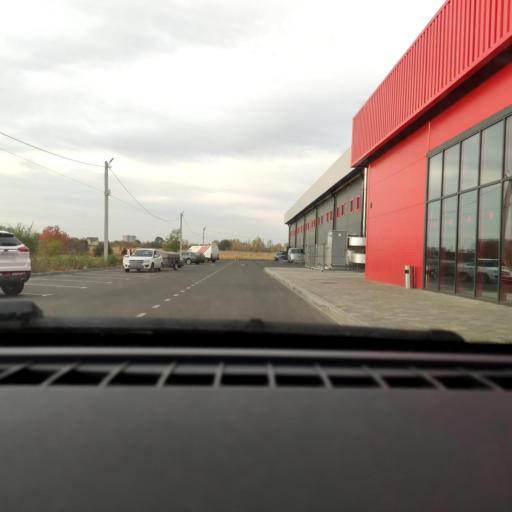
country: RU
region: Voronezj
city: Voronezh
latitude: 51.6789
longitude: 39.2824
